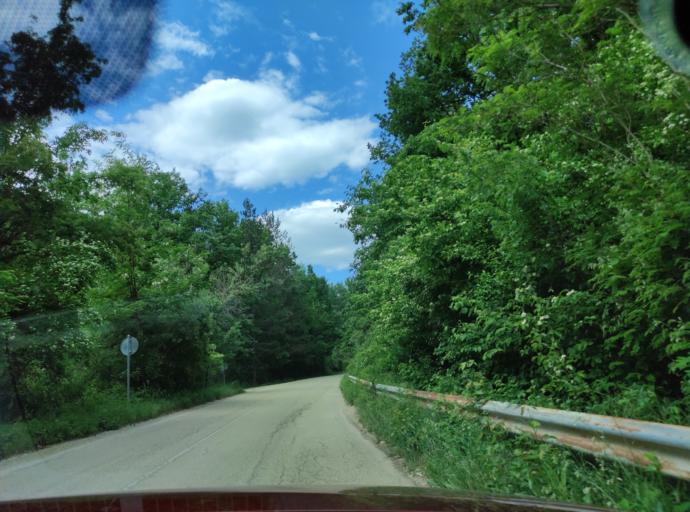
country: BG
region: Montana
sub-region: Obshtina Berkovitsa
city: Berkovitsa
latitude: 43.3761
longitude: 23.0762
